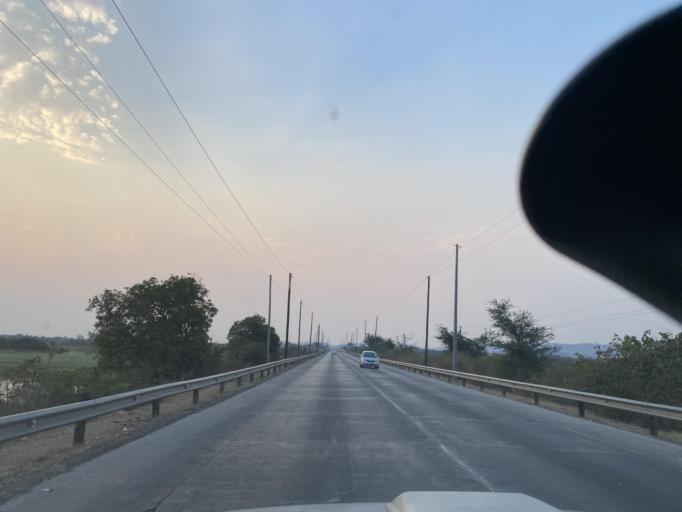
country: ZM
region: Lusaka
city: Kafue
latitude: -15.8408
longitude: 28.2389
